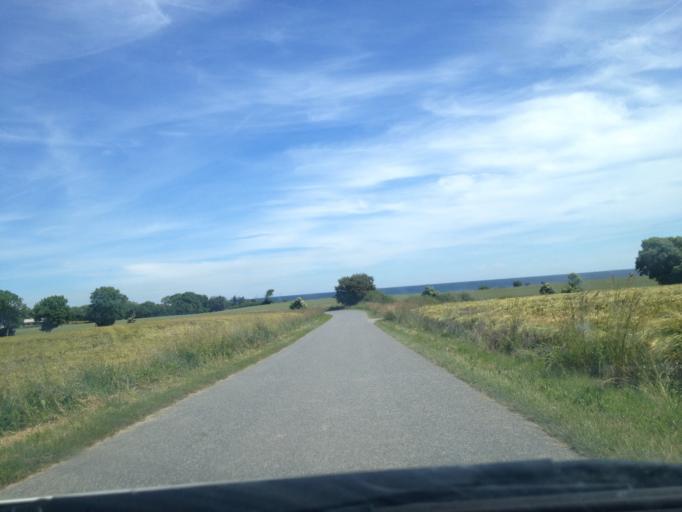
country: DK
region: Central Jutland
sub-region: Samso Kommune
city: Tranebjerg
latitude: 55.8746
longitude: 10.6715
